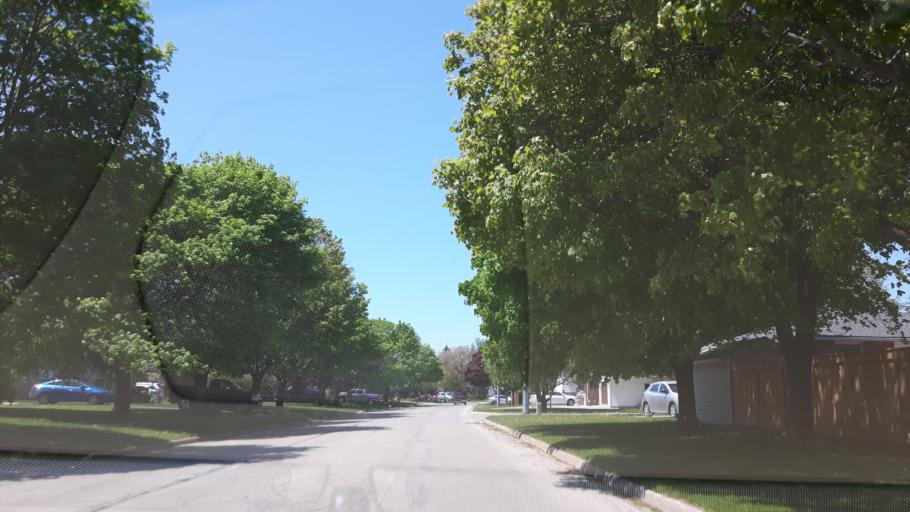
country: CA
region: Ontario
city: Goderich
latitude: 43.7303
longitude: -81.7183
